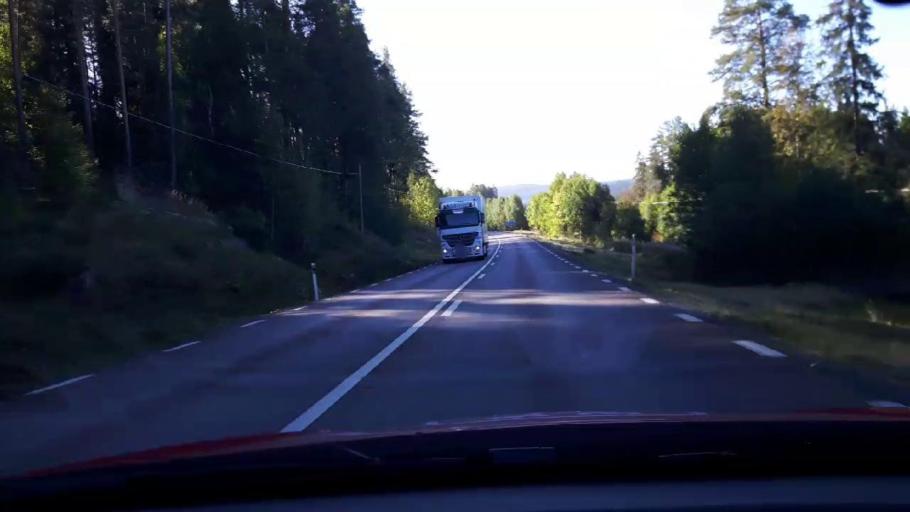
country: SE
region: Jaemtland
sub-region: OEstersunds Kommun
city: Brunflo
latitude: 62.9694
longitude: 15.0203
